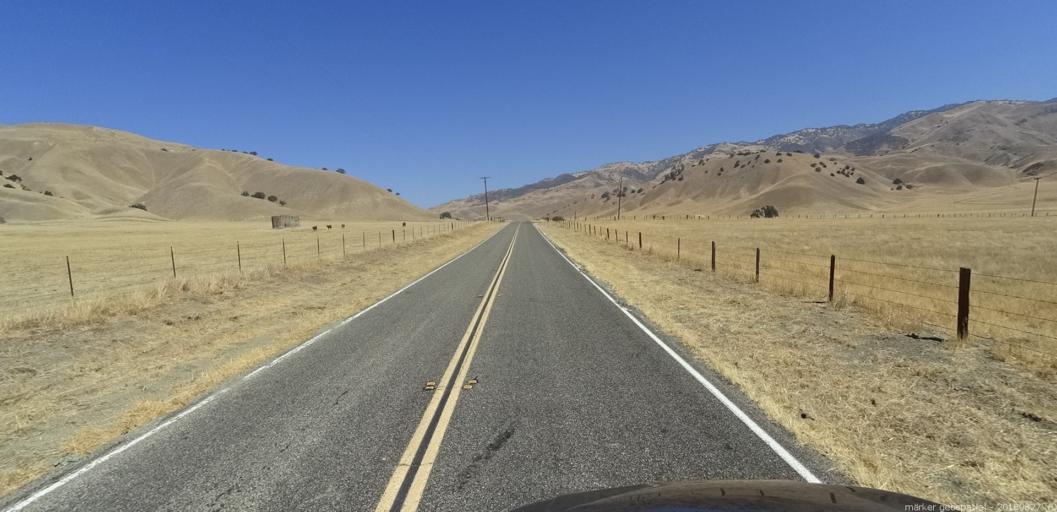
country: US
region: California
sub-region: Monterey County
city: King City
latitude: 36.3081
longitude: -120.9287
